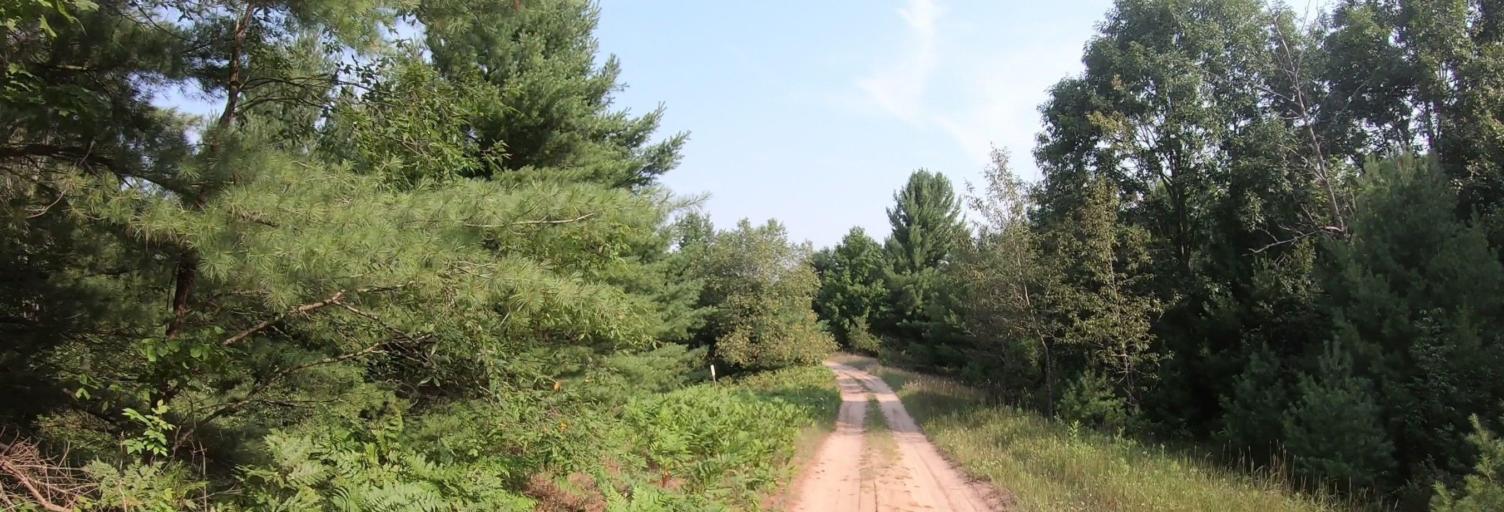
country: US
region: Michigan
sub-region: Benzie County
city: Beulah
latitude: 44.7613
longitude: -85.9260
